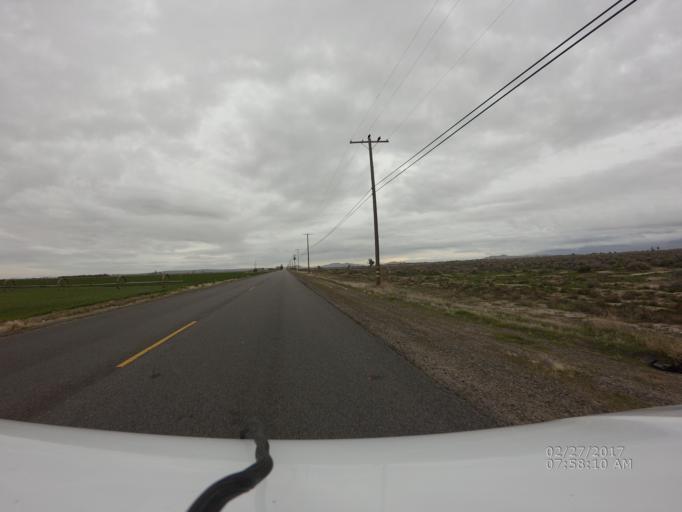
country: US
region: California
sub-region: Los Angeles County
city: Lancaster
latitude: 34.7047
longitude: -117.9986
